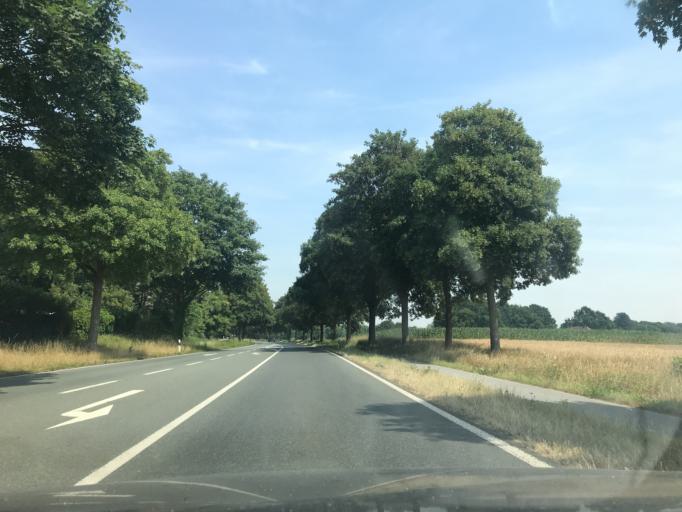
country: DE
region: North Rhine-Westphalia
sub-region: Regierungsbezirk Dusseldorf
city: Issum
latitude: 51.5353
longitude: 6.4335
